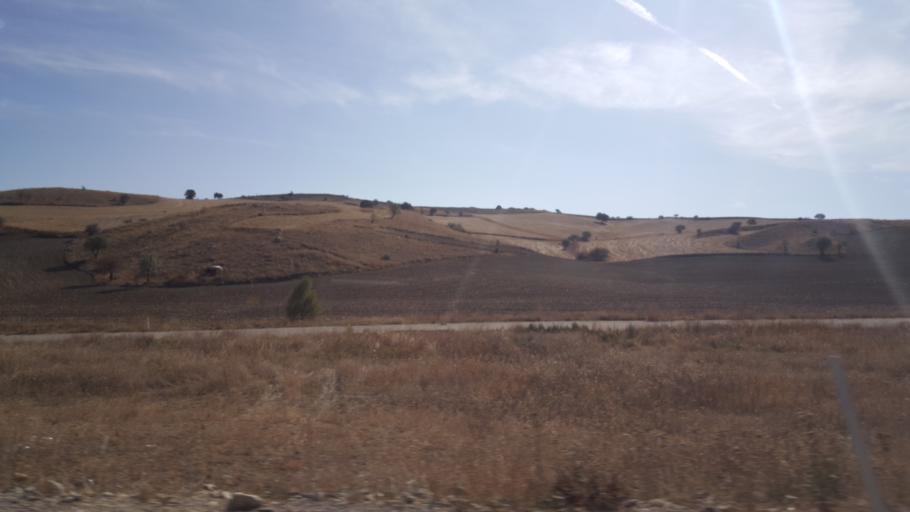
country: TR
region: Ankara
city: Haymana
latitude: 39.4256
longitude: 32.5675
